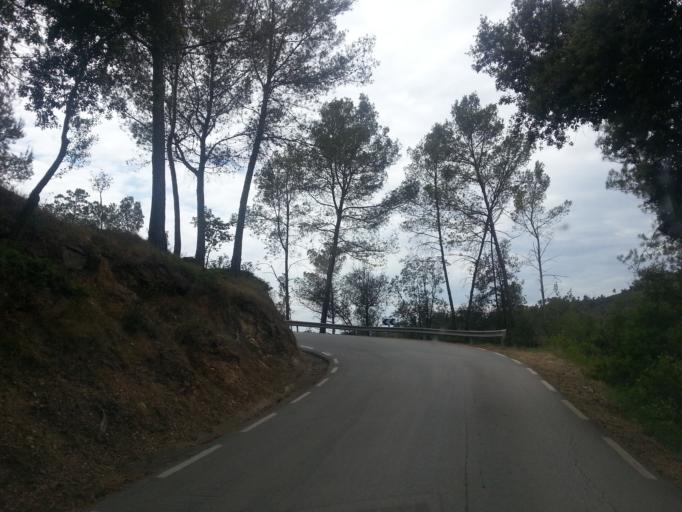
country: ES
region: Catalonia
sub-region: Provincia de Barcelona
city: Molins de Rei
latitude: 41.4322
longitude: 2.0389
